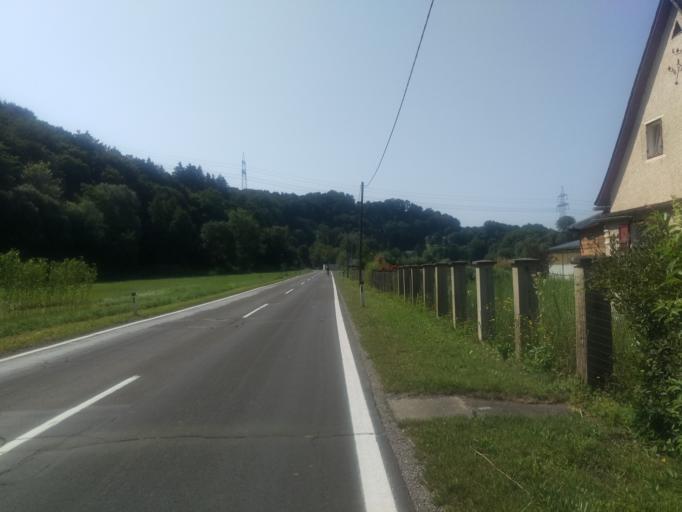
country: AT
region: Styria
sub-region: Politischer Bezirk Graz-Umgebung
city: Mellach
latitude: 46.9486
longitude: 15.5090
